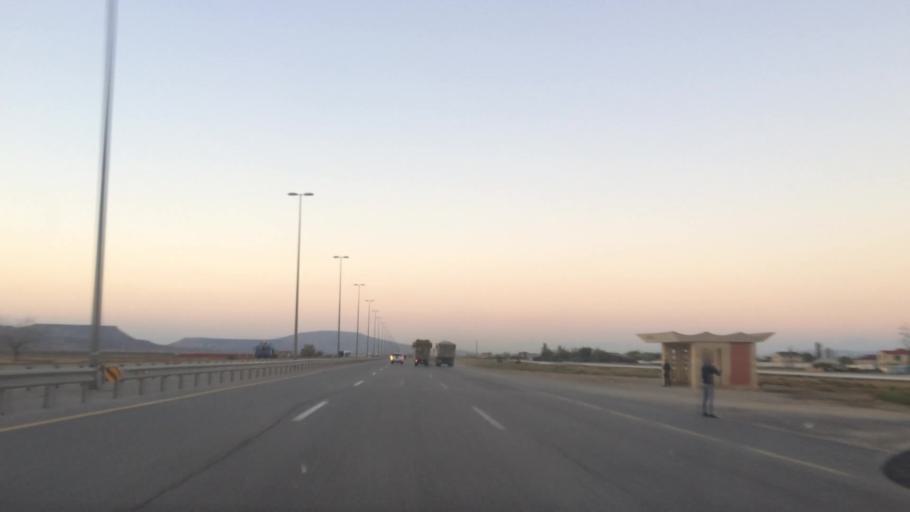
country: AZ
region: Baki
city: Qobustan
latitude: 40.0166
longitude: 49.4260
